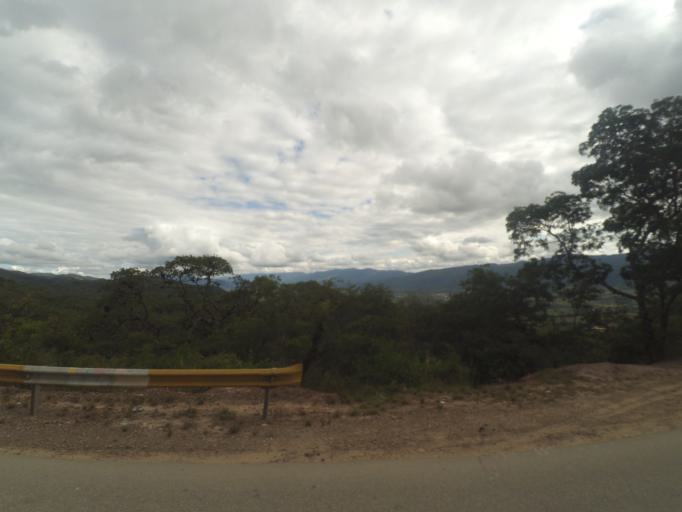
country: BO
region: Santa Cruz
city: Samaipata
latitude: -18.1730
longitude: -63.8779
